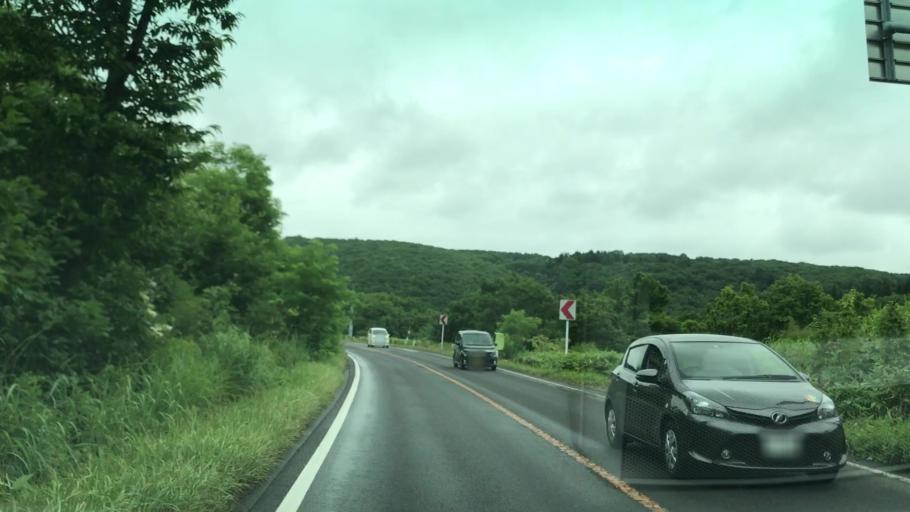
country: JP
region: Hokkaido
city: Muroran
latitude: 42.3826
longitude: 140.9655
